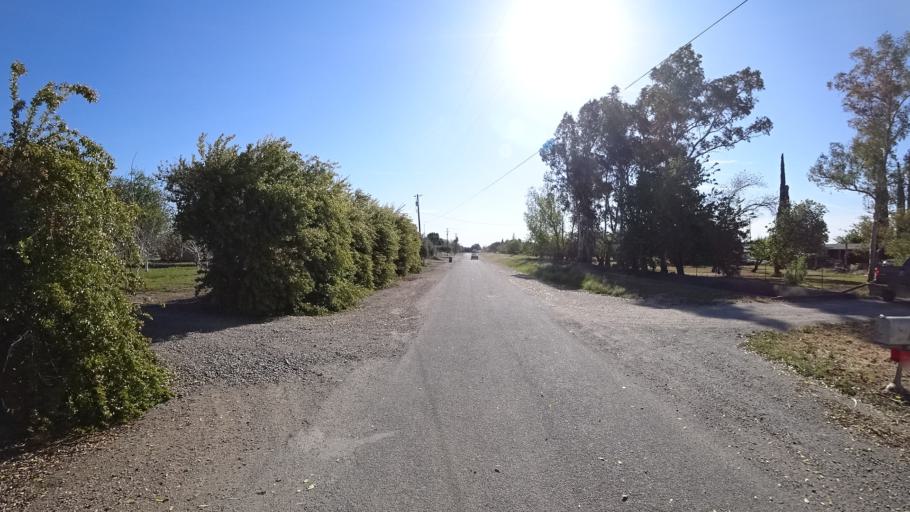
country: US
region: California
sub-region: Glenn County
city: Orland
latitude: 39.7150
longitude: -122.2027
